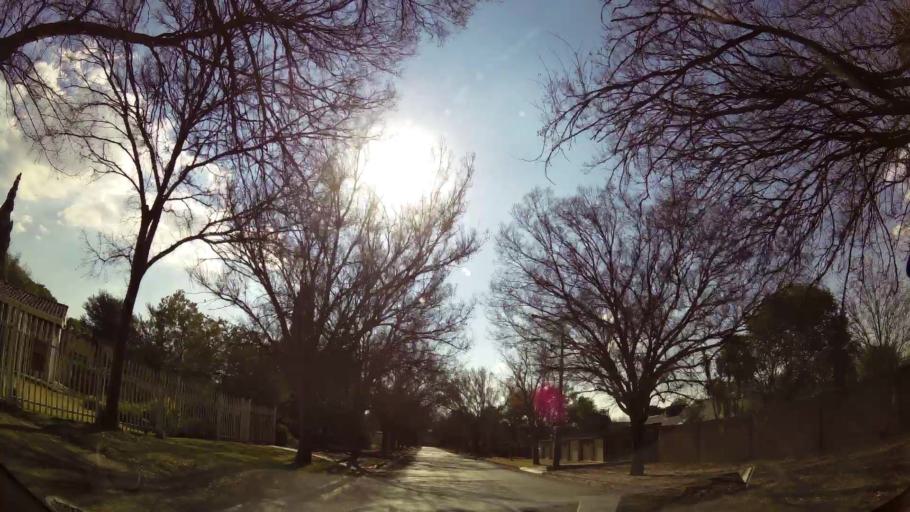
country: ZA
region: Gauteng
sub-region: Ekurhuleni Metropolitan Municipality
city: Benoni
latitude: -26.1432
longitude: 28.3469
